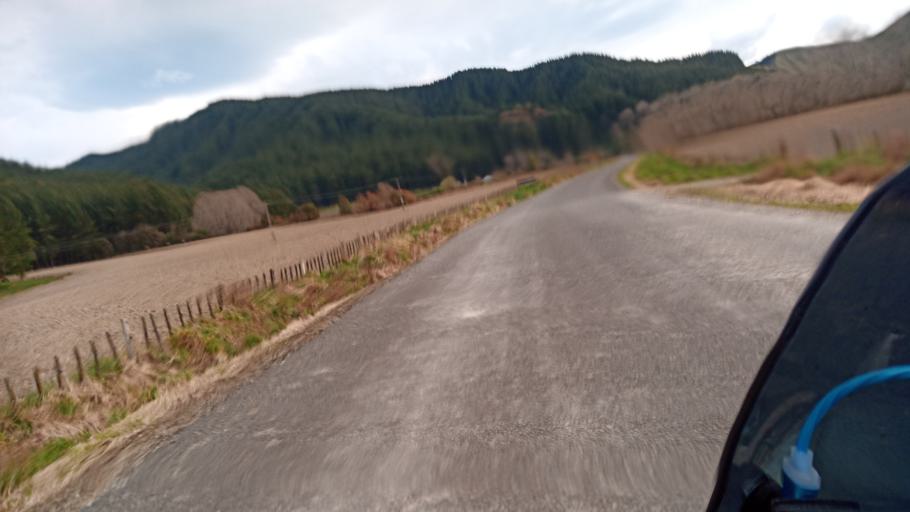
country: NZ
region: Hawke's Bay
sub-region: Wairoa District
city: Wairoa
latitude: -38.8193
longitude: 177.4814
